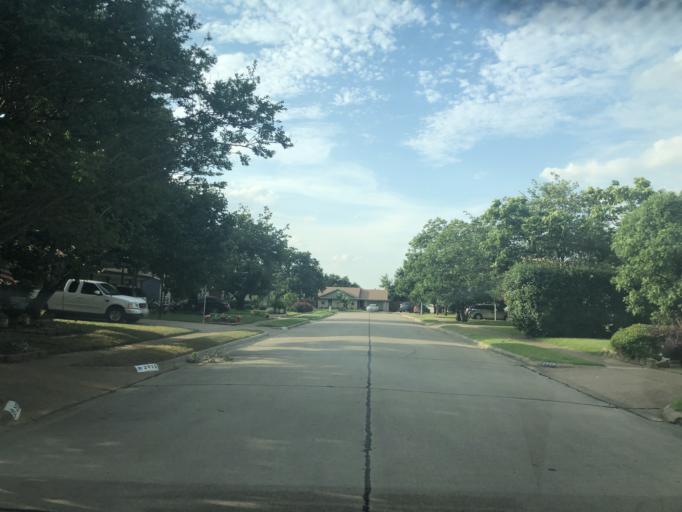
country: US
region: Texas
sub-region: Dallas County
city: Irving
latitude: 32.7878
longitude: -96.9681
